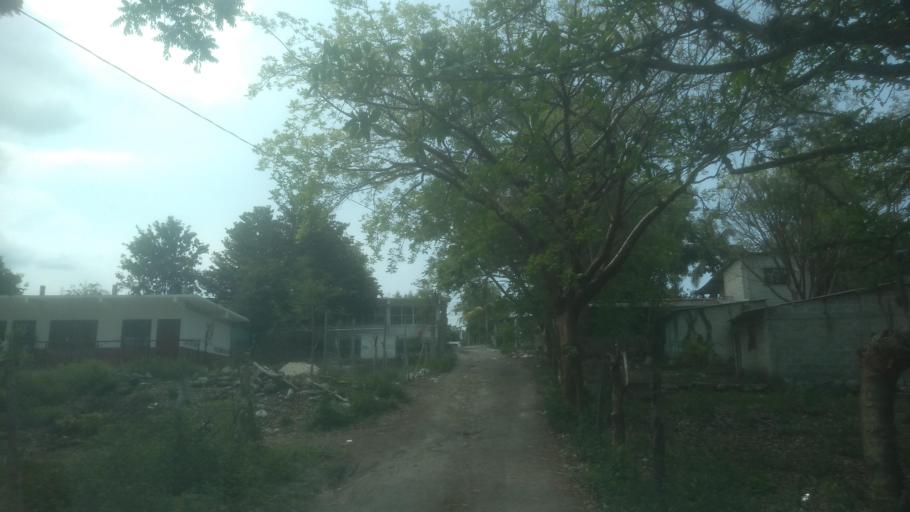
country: MX
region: Veracruz
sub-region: Emiliano Zapata
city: Plan del Rio
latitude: 19.3906
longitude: -96.6346
